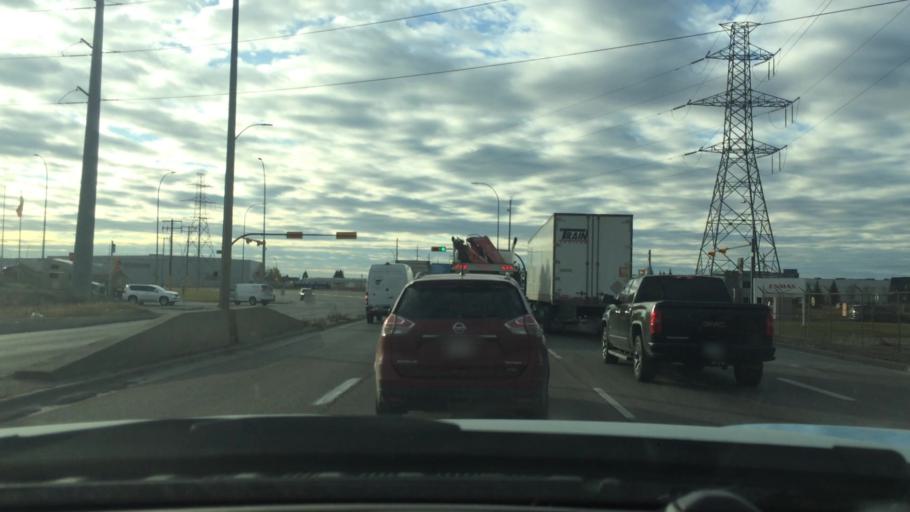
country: CA
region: Alberta
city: Calgary
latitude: 51.0094
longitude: -114.0019
